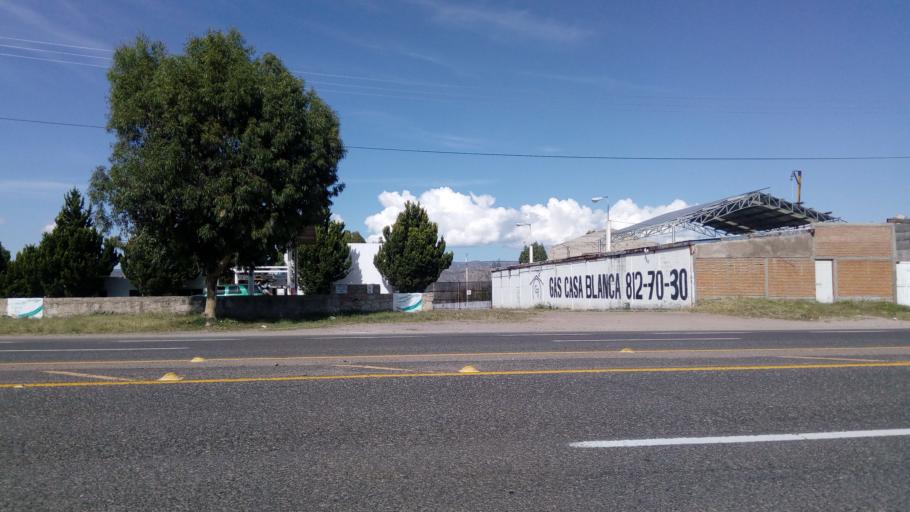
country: MX
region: Durango
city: Victoria de Durango
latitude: 24.1476
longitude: -104.7091
